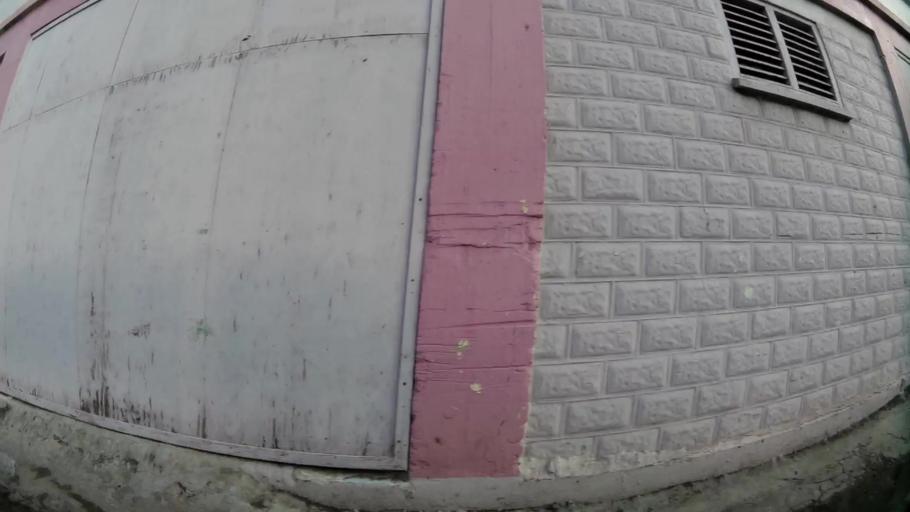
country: KN
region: Saint George Basseterre
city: Basseterre
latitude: 17.2948
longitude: -62.7219
